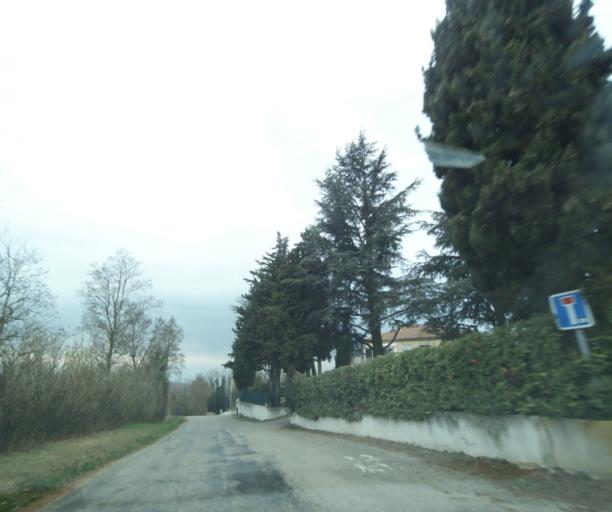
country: FR
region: Rhone-Alpes
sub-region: Departement de la Drome
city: Bourg-les-Valence
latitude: 44.9777
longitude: 4.9193
